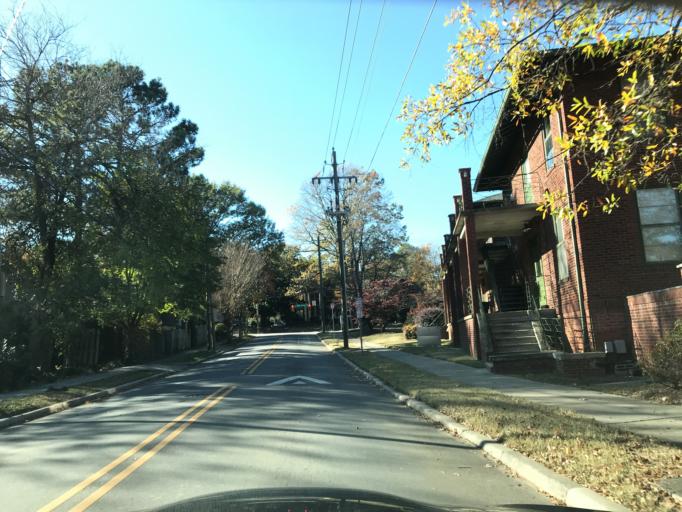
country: US
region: North Carolina
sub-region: Wake County
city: Raleigh
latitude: 35.7932
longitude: -78.6310
